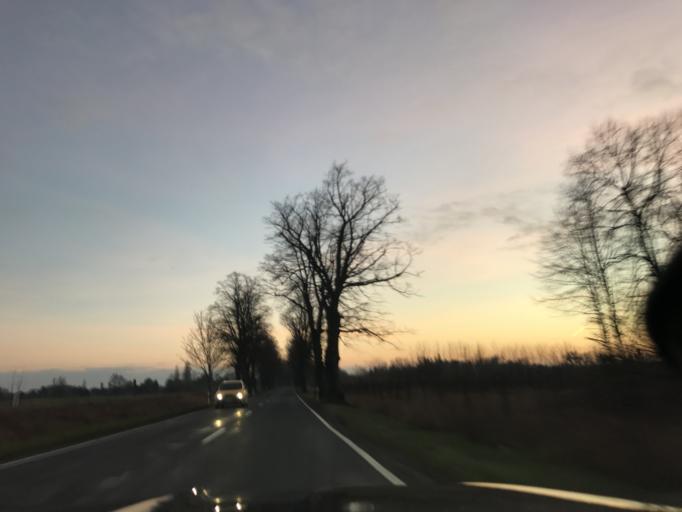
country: DE
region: Brandenburg
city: Ketzin
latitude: 52.4935
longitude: 12.8507
